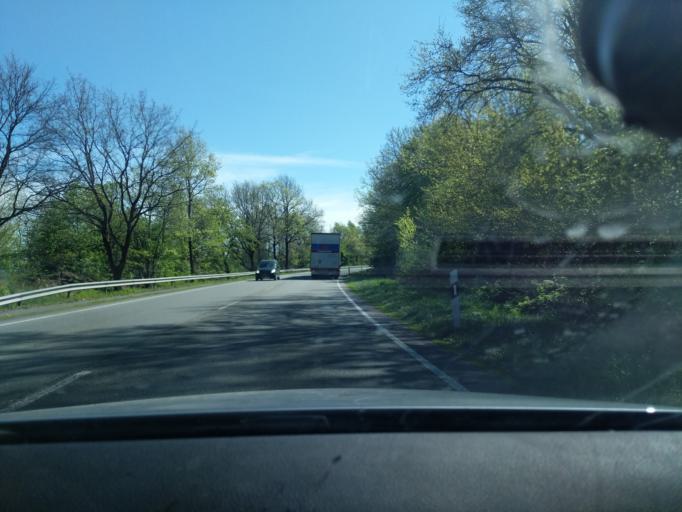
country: DE
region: Lower Saxony
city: Buxtehude
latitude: 53.4614
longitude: 9.7101
